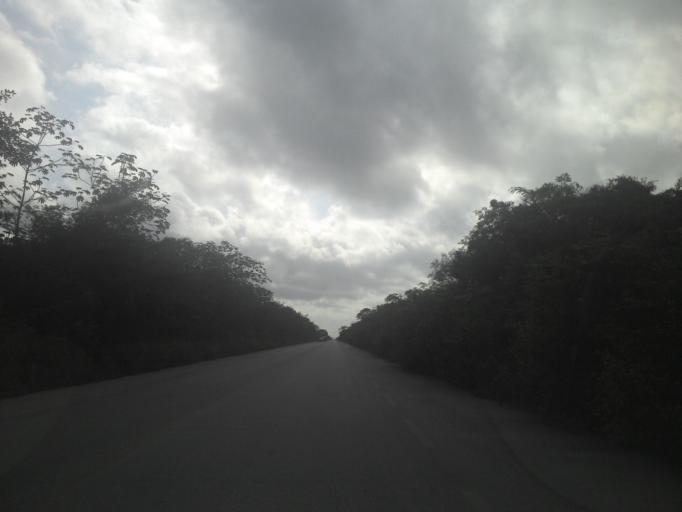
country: MX
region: Quintana Roo
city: Coba
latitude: 20.5404
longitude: -87.7830
